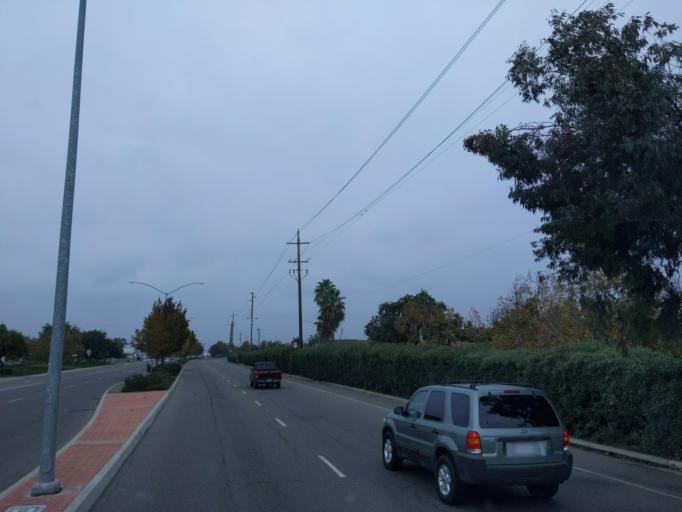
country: US
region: California
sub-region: San Joaquin County
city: Kennedy
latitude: 37.9206
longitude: -121.2625
